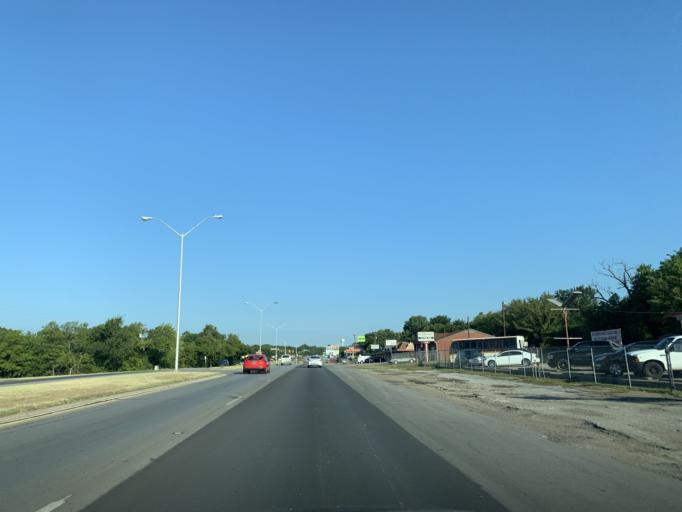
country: US
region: Texas
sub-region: Tarrant County
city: Sansom Park
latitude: 32.7952
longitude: -97.3958
